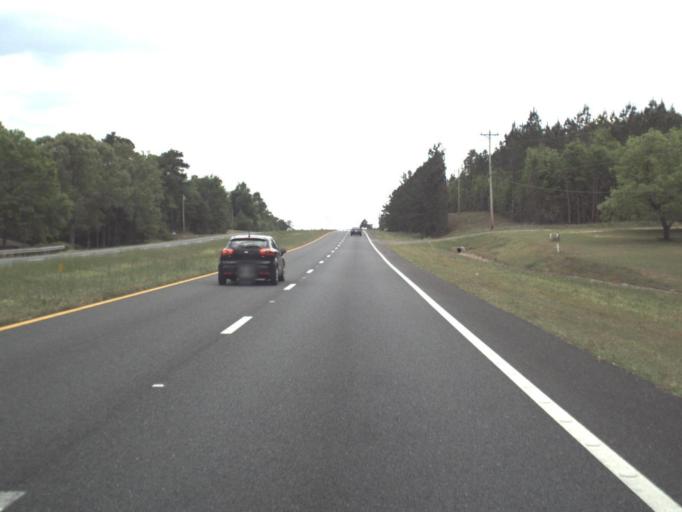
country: US
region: Florida
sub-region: Escambia County
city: Century
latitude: 30.8817
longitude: -87.3218
